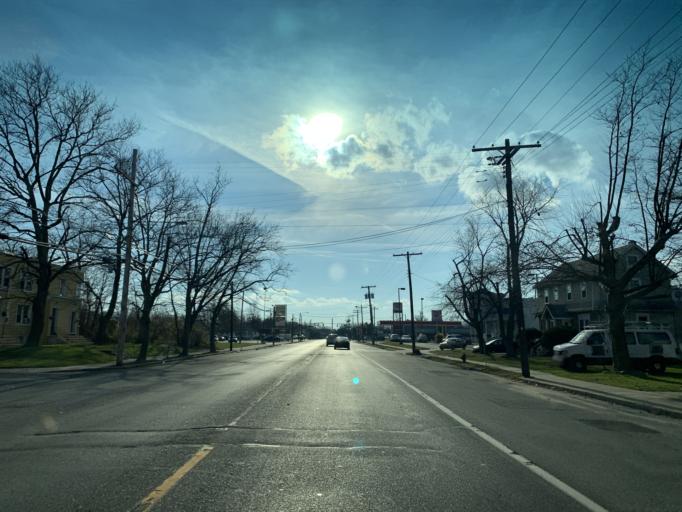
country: US
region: New Jersey
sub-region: Salem County
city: Penns Grove
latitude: 39.7276
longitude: -75.4631
